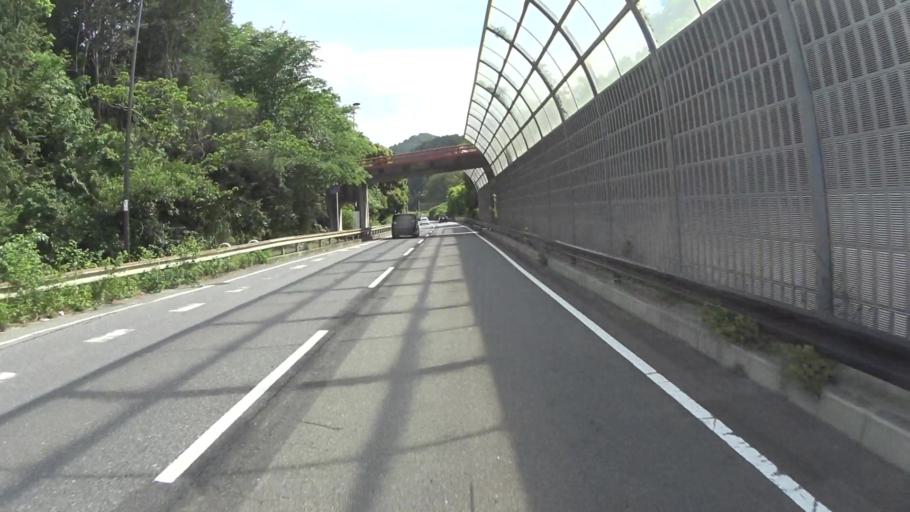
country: JP
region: Shiga Prefecture
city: Otsu-shi
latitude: 35.0247
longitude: 135.8495
